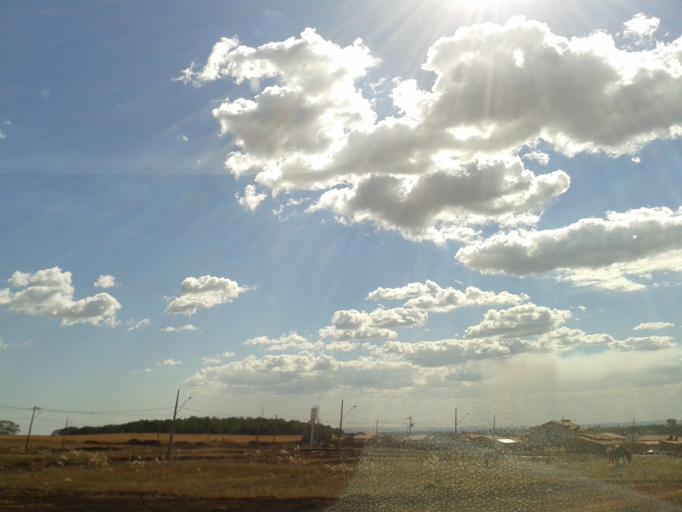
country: BR
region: Minas Gerais
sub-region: Capinopolis
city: Capinopolis
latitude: -18.6947
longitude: -49.5751
